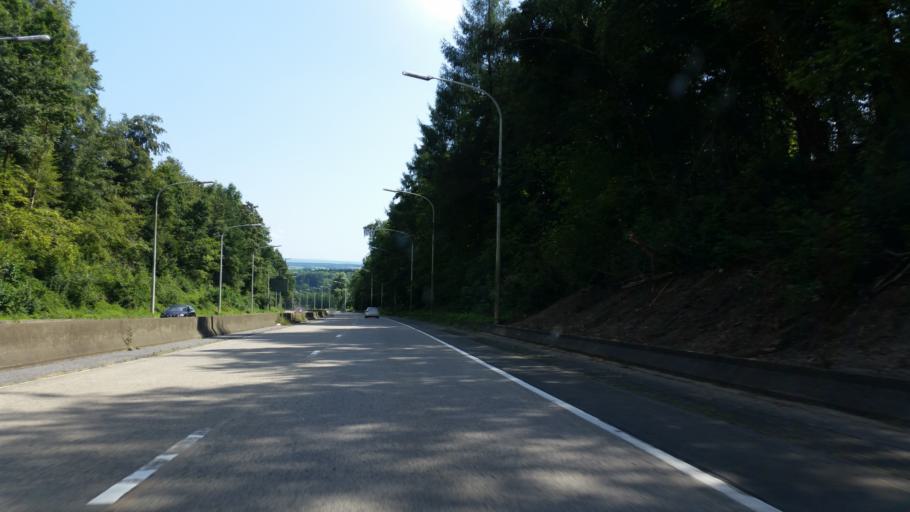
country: BE
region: Wallonia
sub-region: Province de Namur
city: Hamois
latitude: 50.2818
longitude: 5.1908
